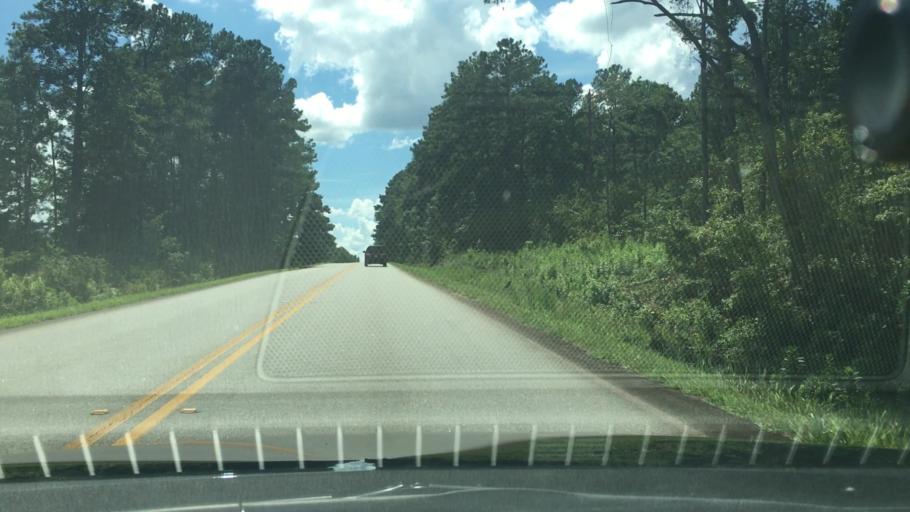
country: US
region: Georgia
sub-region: Jasper County
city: Monticello
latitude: 33.3048
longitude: -83.6155
